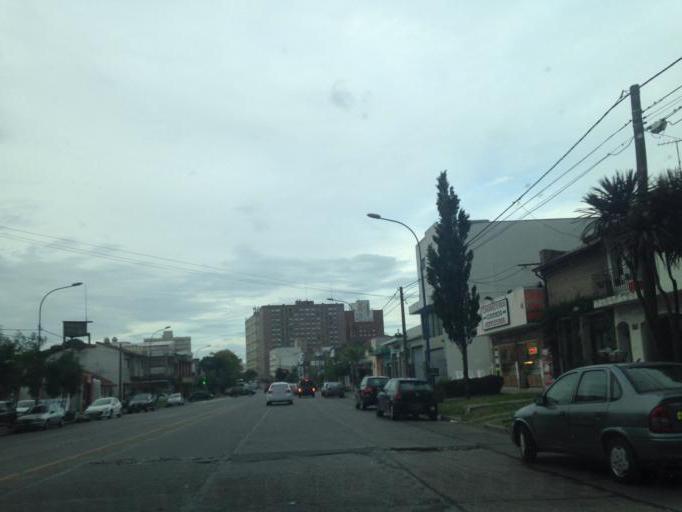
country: AR
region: Buenos Aires
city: Mar del Plata
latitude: -38.0204
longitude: -57.5729
